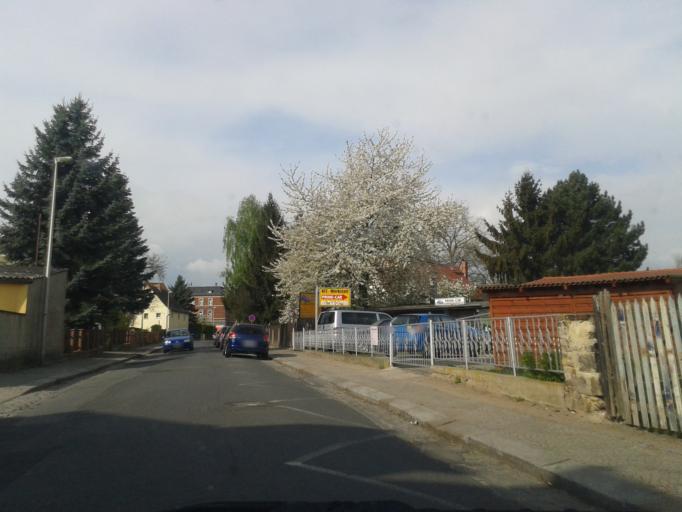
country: DE
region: Saxony
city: Radebeul
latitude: 51.0968
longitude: 13.6622
